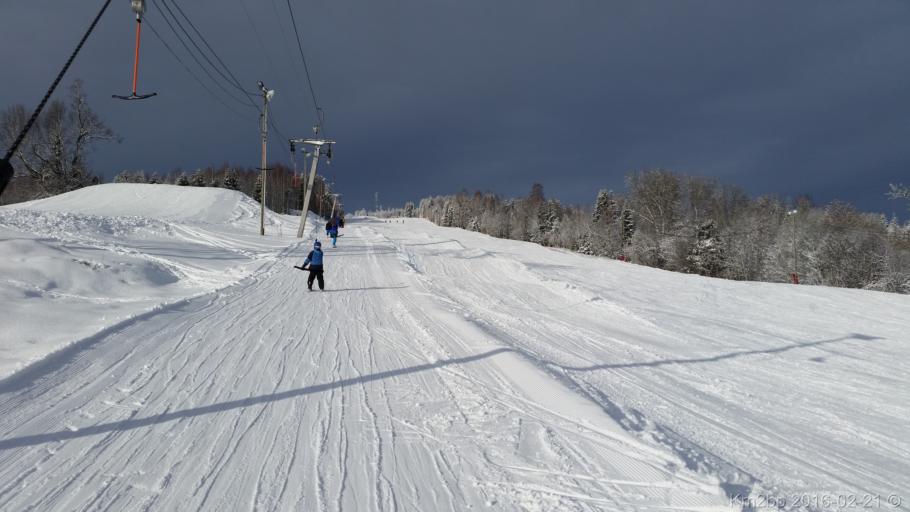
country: NO
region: Akershus
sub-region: Nannestad
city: Maura
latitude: 60.2635
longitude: 11.0226
